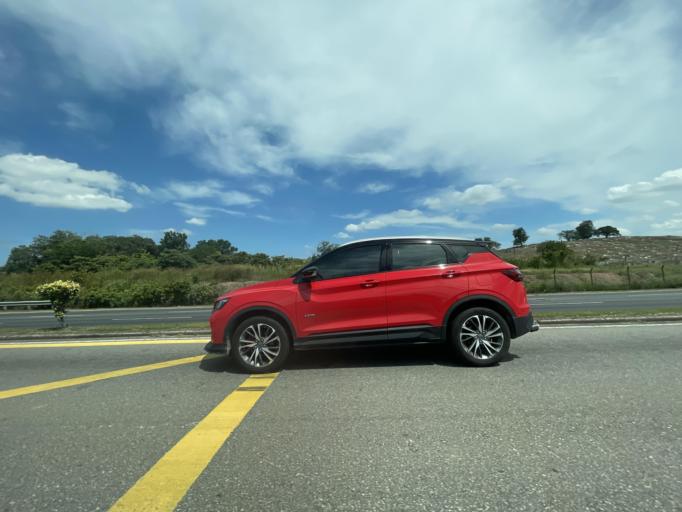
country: MY
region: Melaka
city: Batu Berendam
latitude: 2.2426
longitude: 102.2234
